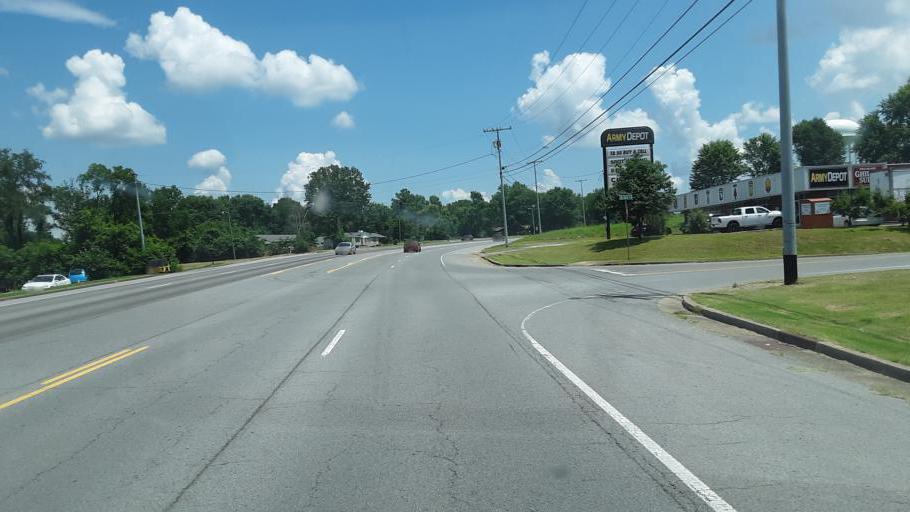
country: US
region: Kentucky
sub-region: Christian County
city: Oak Grove
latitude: 36.6321
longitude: -87.4299
